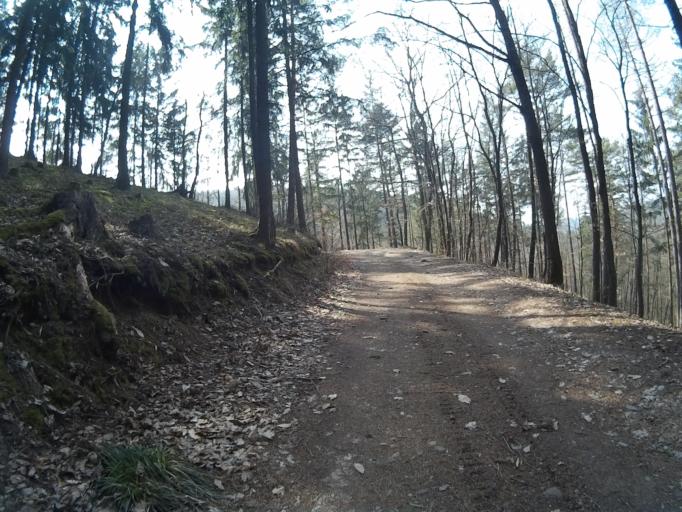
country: CZ
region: South Moravian
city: Pozorice
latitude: 49.2234
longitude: 16.7915
